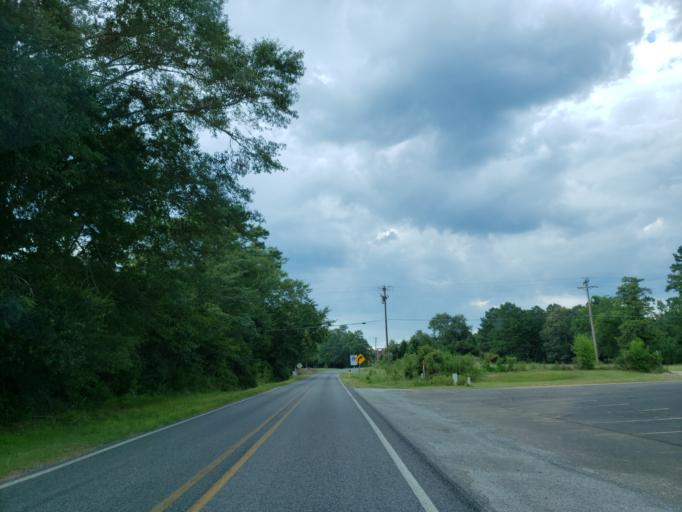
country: US
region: Mississippi
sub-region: Jones County
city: Sharon
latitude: 32.0308
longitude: -89.0377
